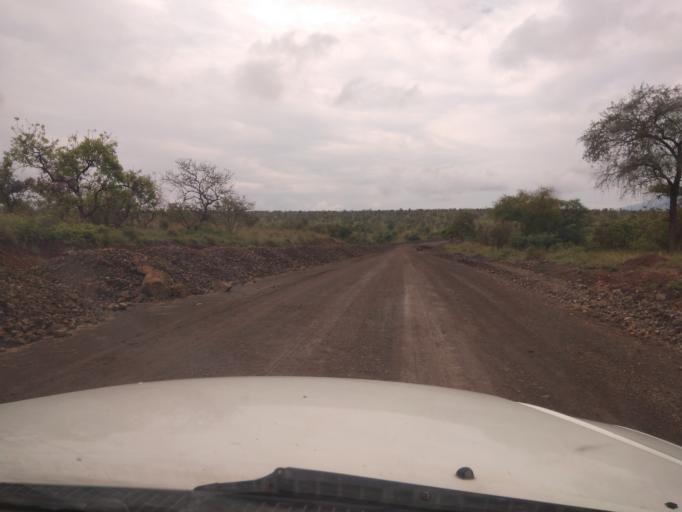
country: ET
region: Southern Nations, Nationalities, and People's Region
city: Felege Neway
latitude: 6.4307
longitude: 37.2641
